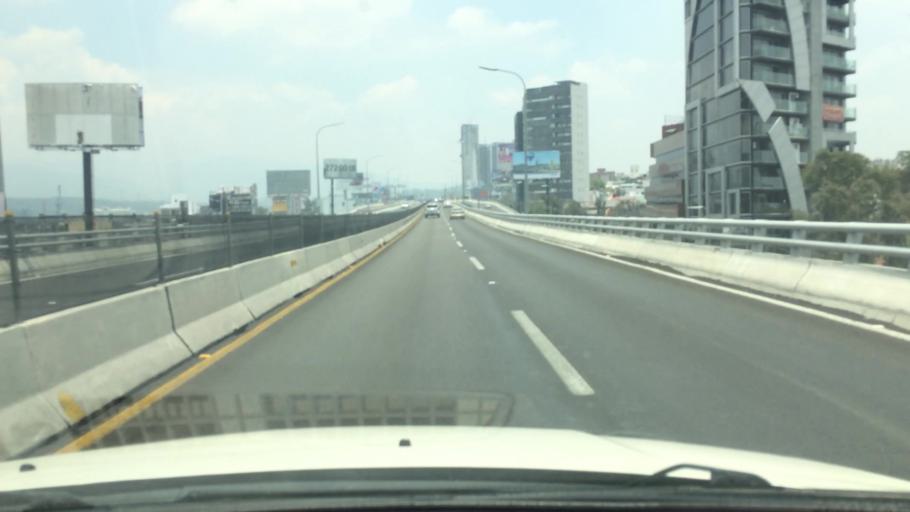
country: MX
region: Mexico City
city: Tlalpan
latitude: 19.3025
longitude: -99.1667
